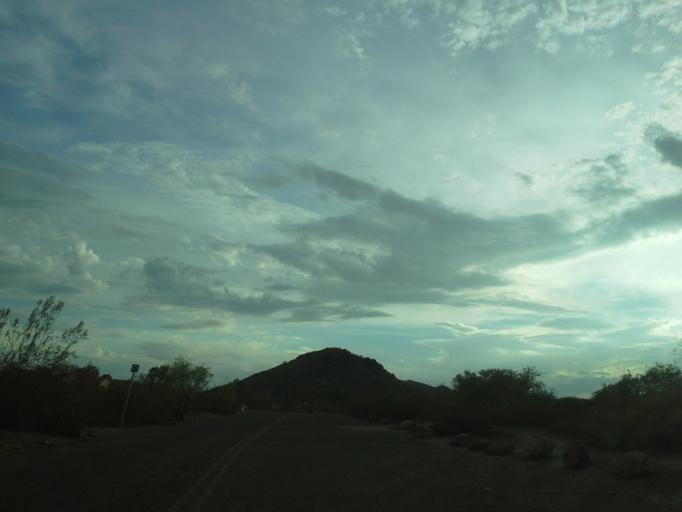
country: US
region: Arizona
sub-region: Maricopa County
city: Guadalupe
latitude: 33.3639
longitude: -111.9805
